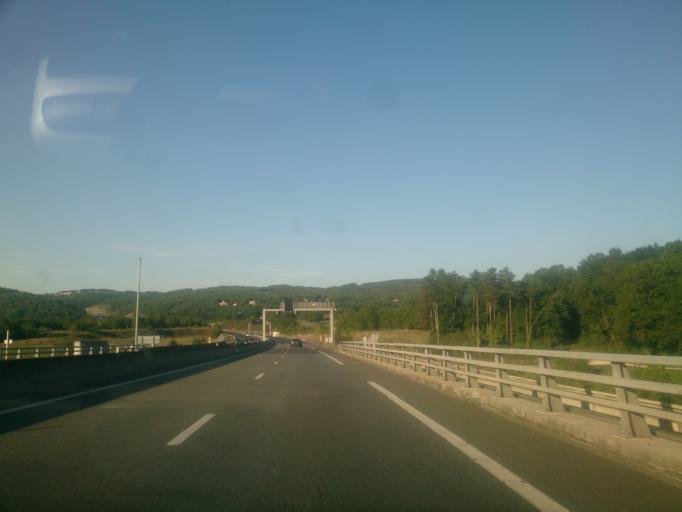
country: FR
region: Midi-Pyrenees
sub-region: Departement du Lot
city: Souillac
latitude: 44.8527
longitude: 1.4962
